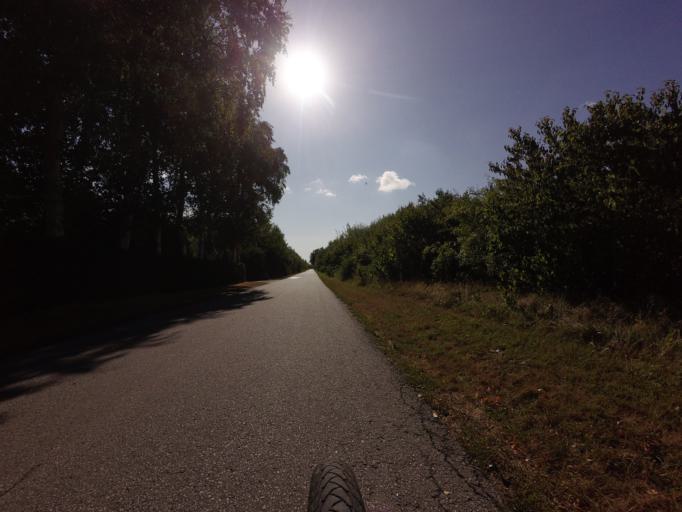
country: DK
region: North Denmark
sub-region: Hjorring Kommune
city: Vra
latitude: 57.3981
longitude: 9.9767
